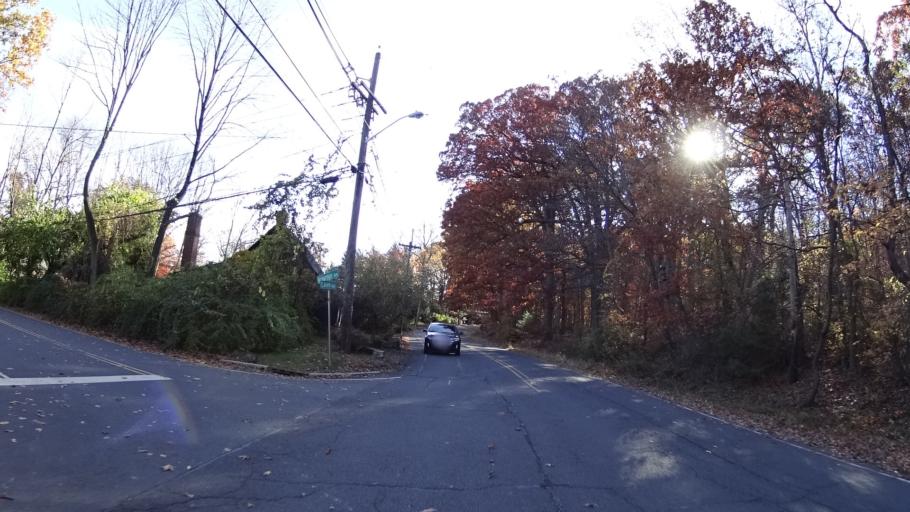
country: US
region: New Jersey
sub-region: Union County
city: Mountainside
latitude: 40.6792
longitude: -74.3741
